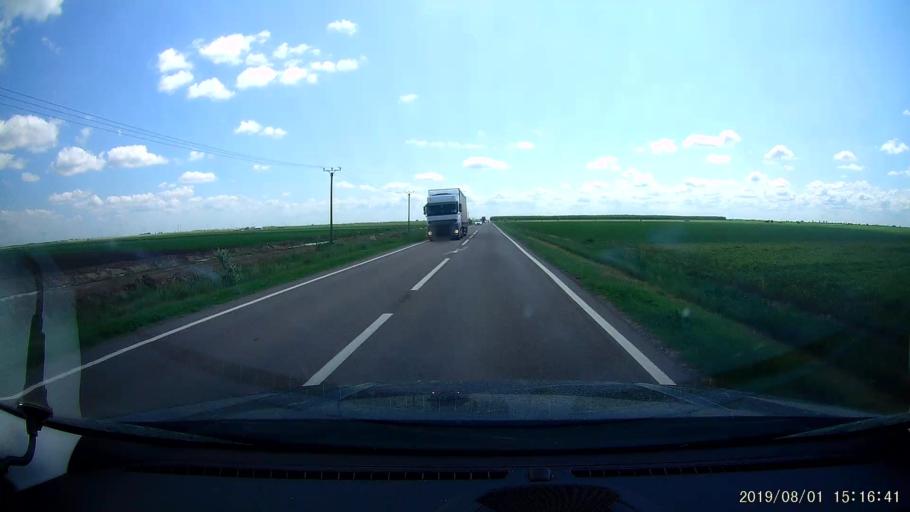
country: RO
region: Braila
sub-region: Comuna Unirea
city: Unirea
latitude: 45.1424
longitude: 27.8487
